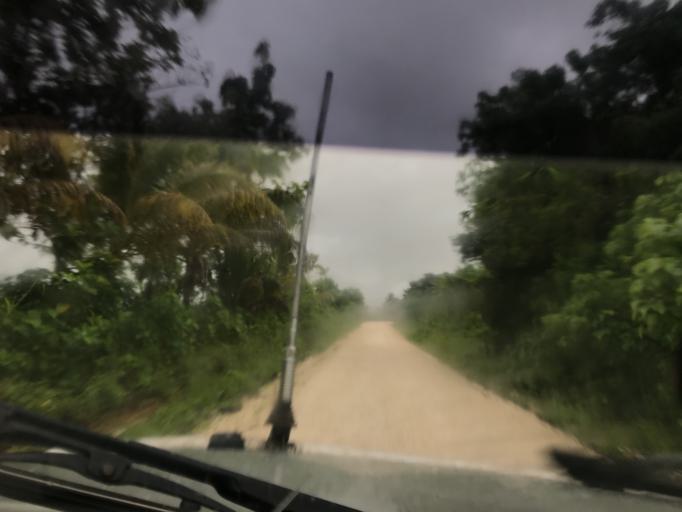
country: SB
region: Malaita
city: Auki
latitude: -9.0253
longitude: 160.7998
